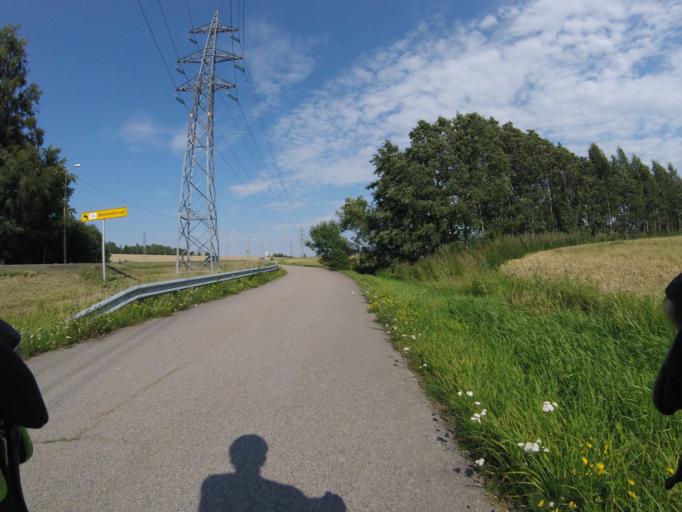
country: NO
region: Akershus
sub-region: Skedsmo
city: Leirsund
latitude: 59.9900
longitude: 11.0757
